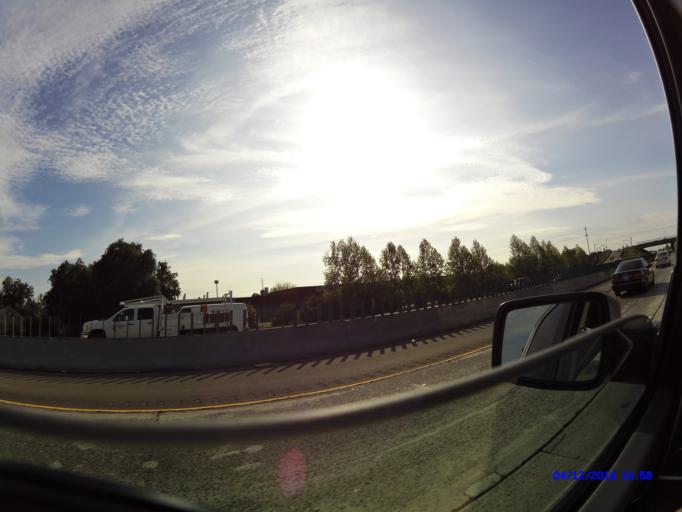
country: US
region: California
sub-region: Stanislaus County
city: Modesto
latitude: 37.6639
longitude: -121.0282
